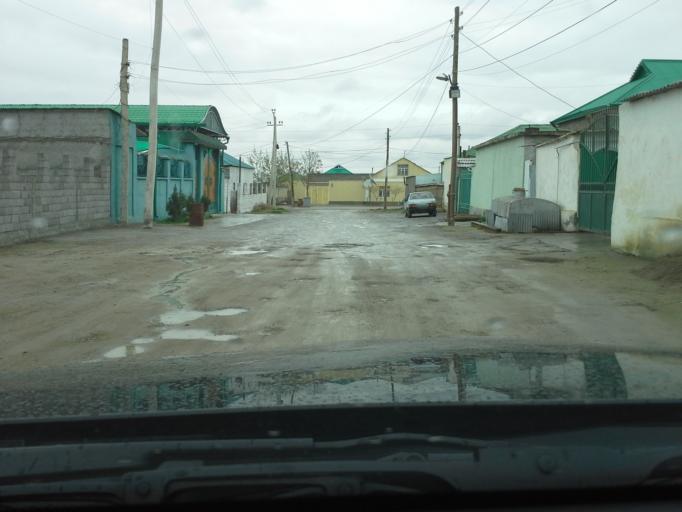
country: TM
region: Ahal
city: Abadan
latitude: 37.9702
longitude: 58.2106
